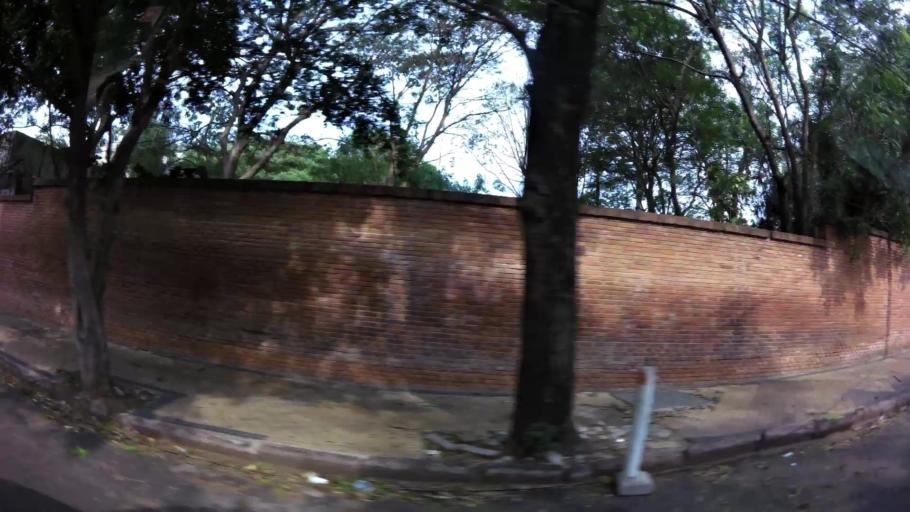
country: PY
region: Asuncion
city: Asuncion
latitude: -25.2882
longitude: -57.6131
